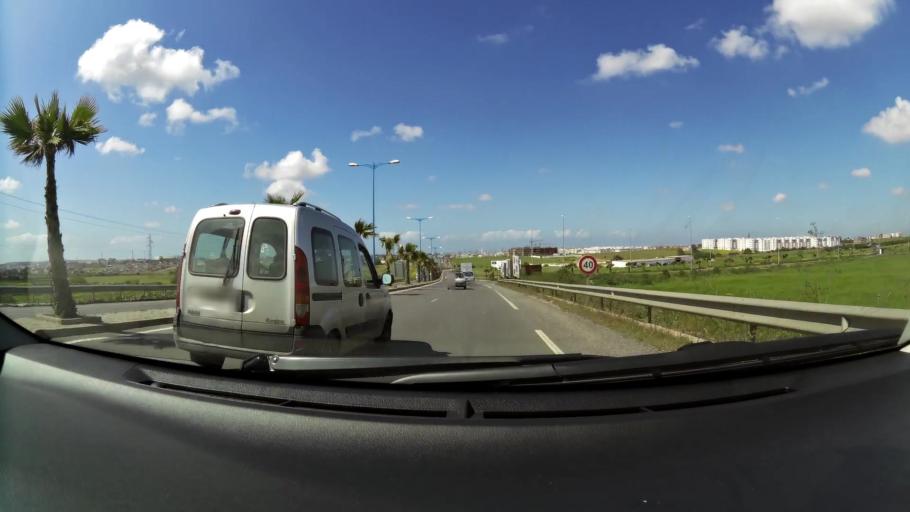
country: MA
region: Grand Casablanca
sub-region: Nouaceur
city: Bouskoura
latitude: 33.5125
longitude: -7.6131
